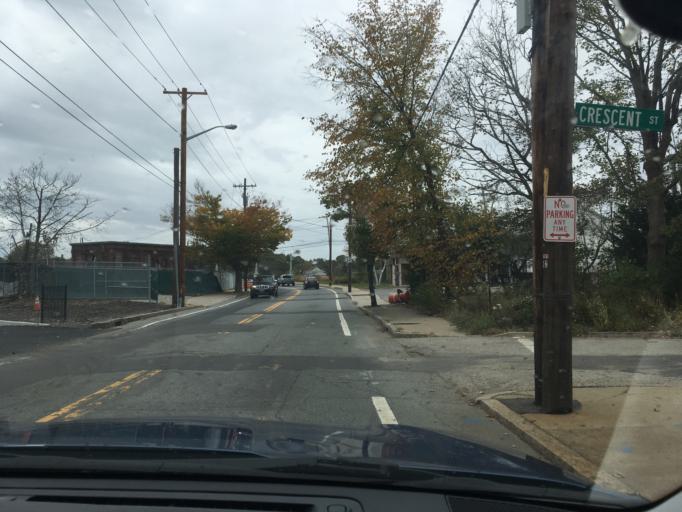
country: US
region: Rhode Island
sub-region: Bristol County
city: Warren
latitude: 41.7367
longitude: -71.2868
